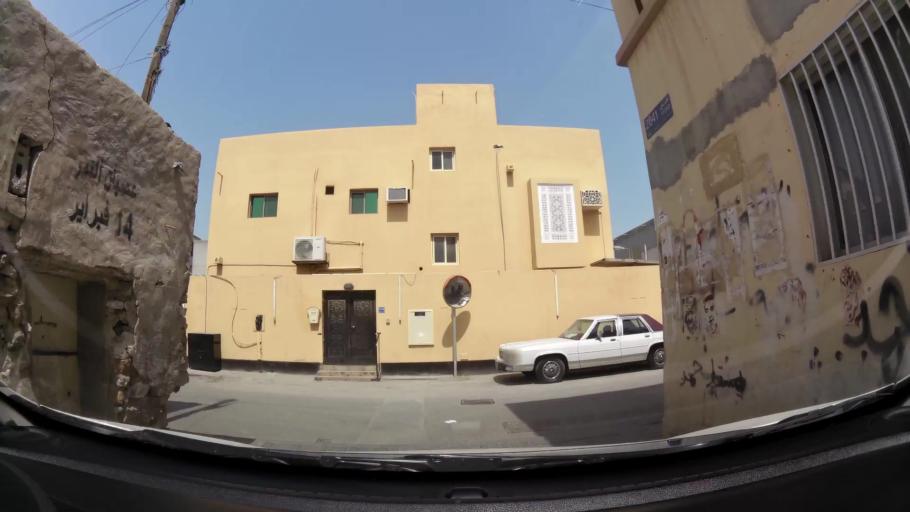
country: BH
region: Manama
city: Jidd Hafs
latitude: 26.2306
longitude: 50.4819
